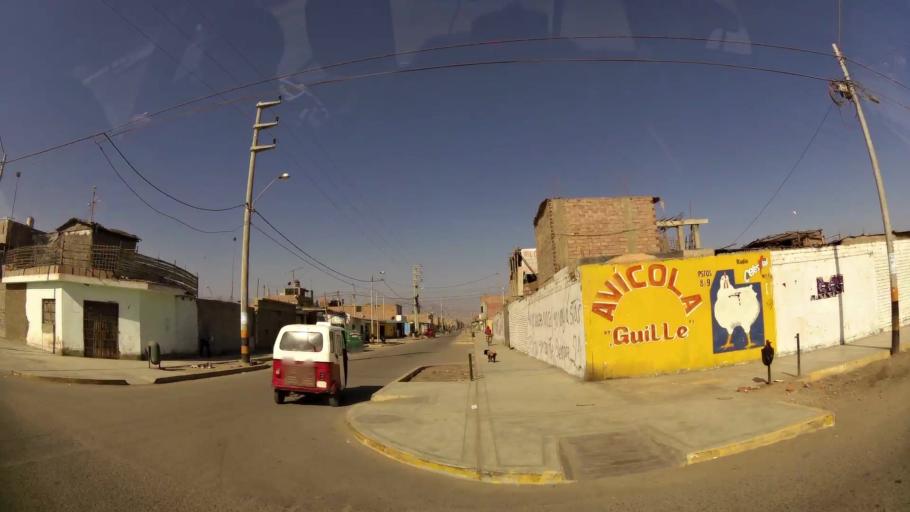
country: PE
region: Ica
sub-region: Provincia de Chincha
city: Chincha Alta
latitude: -13.4047
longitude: -76.1250
